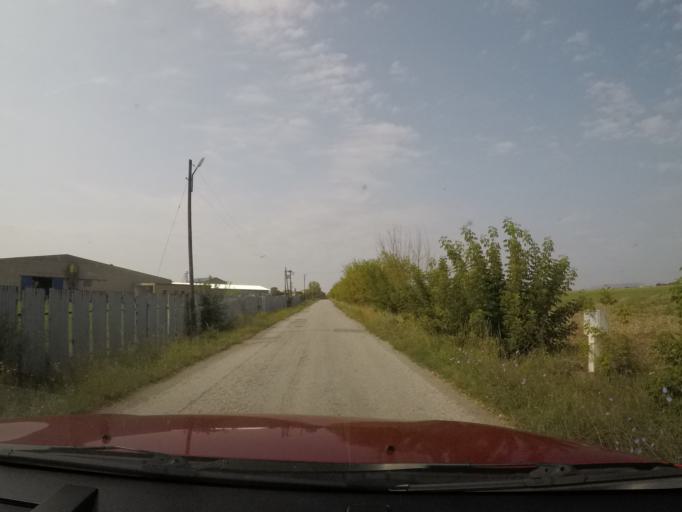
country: SK
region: Kosicky
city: Moldava nad Bodvou
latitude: 48.5900
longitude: 21.0176
